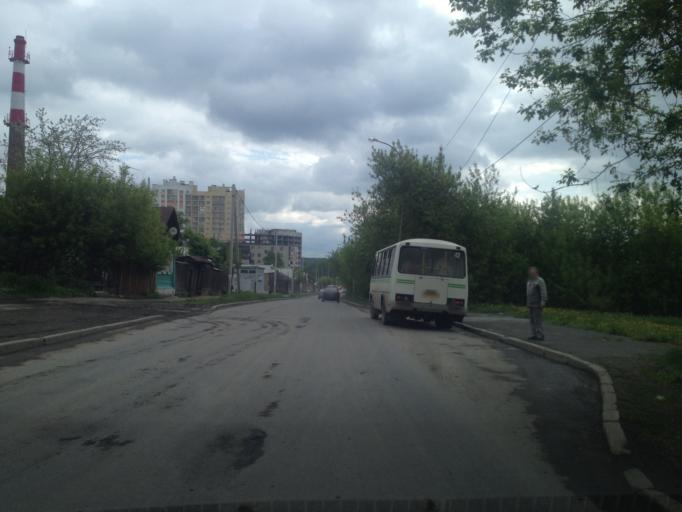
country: RU
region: Sverdlovsk
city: Yekaterinburg
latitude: 56.7802
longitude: 60.6507
